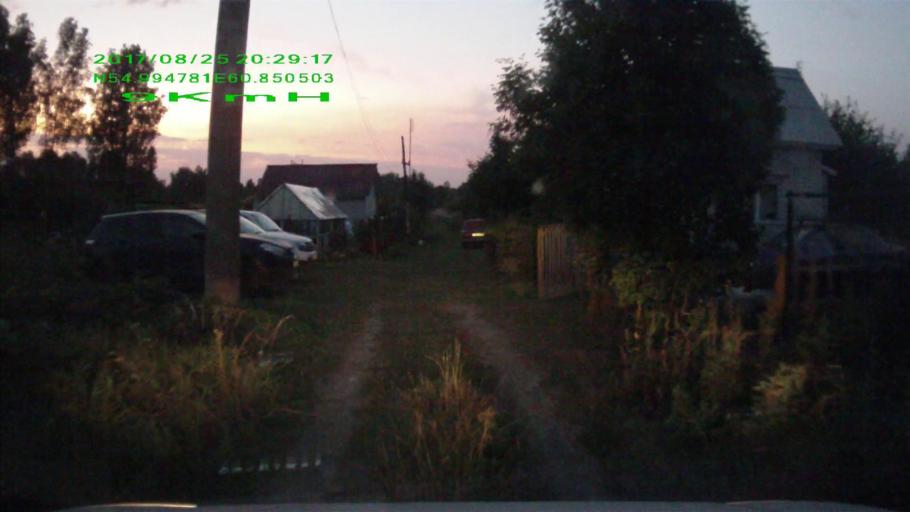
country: RU
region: Chelyabinsk
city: Timiryazevskiy
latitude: 54.9948
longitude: 60.8505
